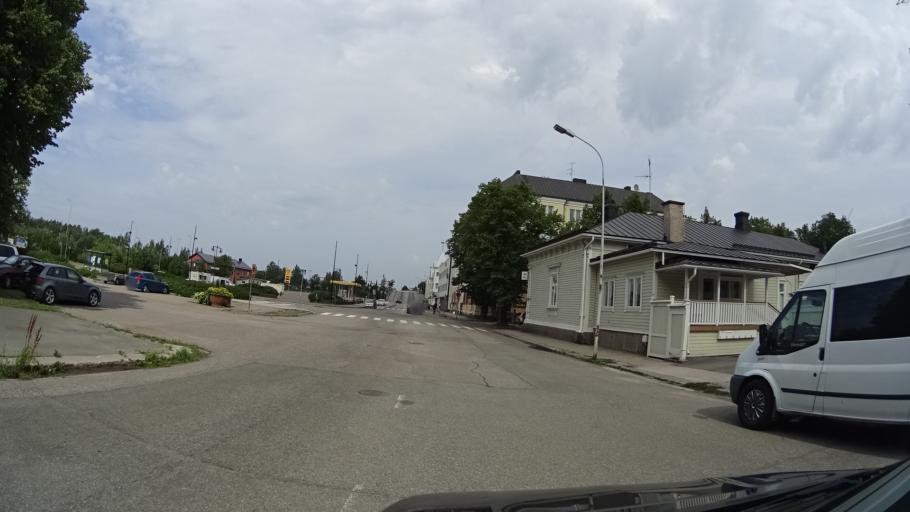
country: FI
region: Uusimaa
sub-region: Raaseporin
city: Hanko
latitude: 59.8238
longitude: 22.9637
